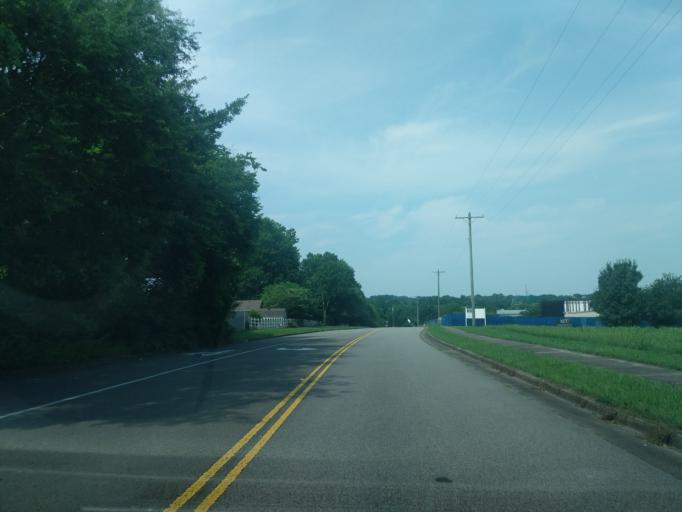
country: US
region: Tennessee
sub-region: Davidson County
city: Lakewood
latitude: 36.2653
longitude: -86.6646
